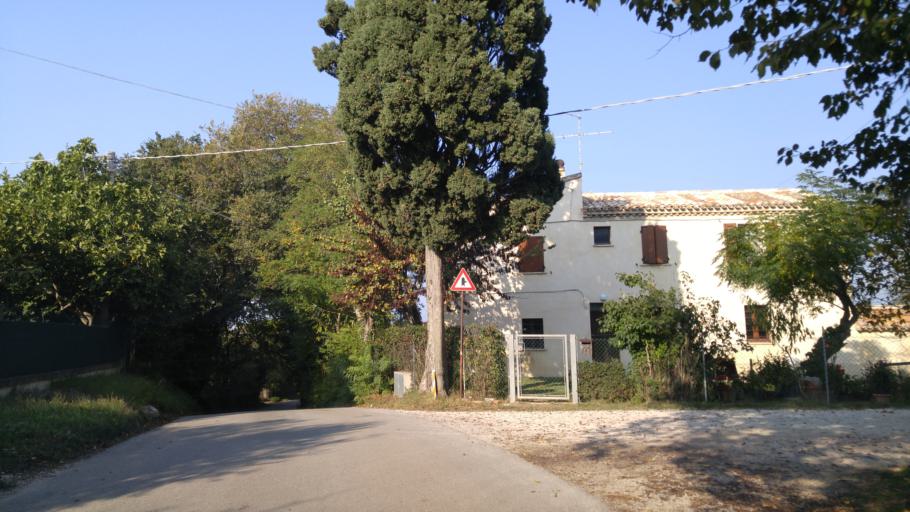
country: IT
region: The Marches
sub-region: Provincia di Pesaro e Urbino
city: Fenile
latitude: 43.8661
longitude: 12.9655
